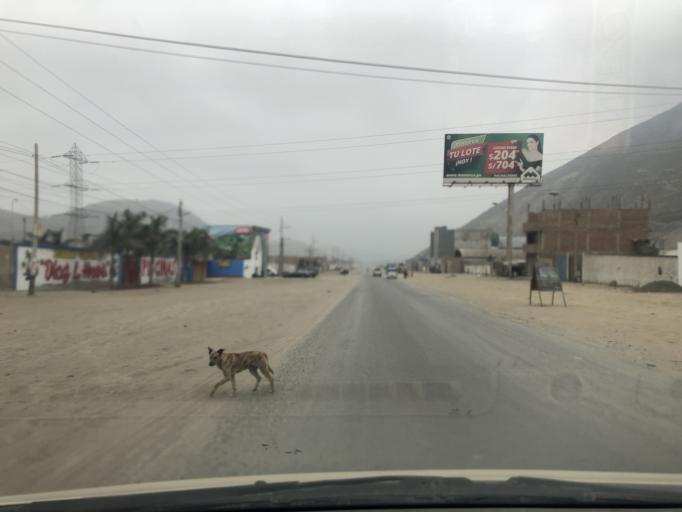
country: PE
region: Lima
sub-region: Lima
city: Cieneguilla
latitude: -12.1554
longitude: -76.8690
